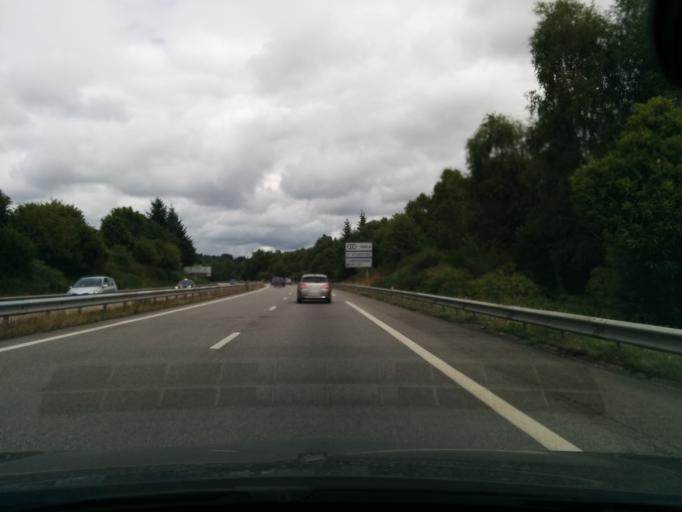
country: FR
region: Limousin
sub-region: Departement de la Haute-Vienne
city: Compreignac
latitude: 45.9771
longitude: 1.3245
